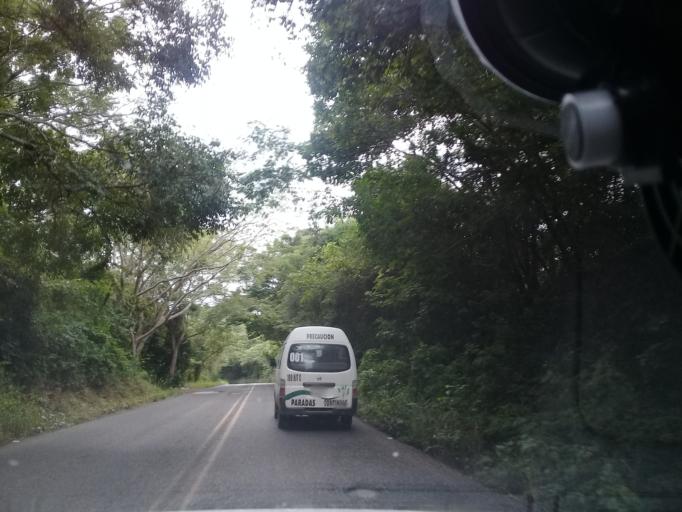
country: MX
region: Hidalgo
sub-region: Huejutla de Reyes
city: Parque de Poblamiento Solidaridad
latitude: 21.1938
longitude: -98.3941
